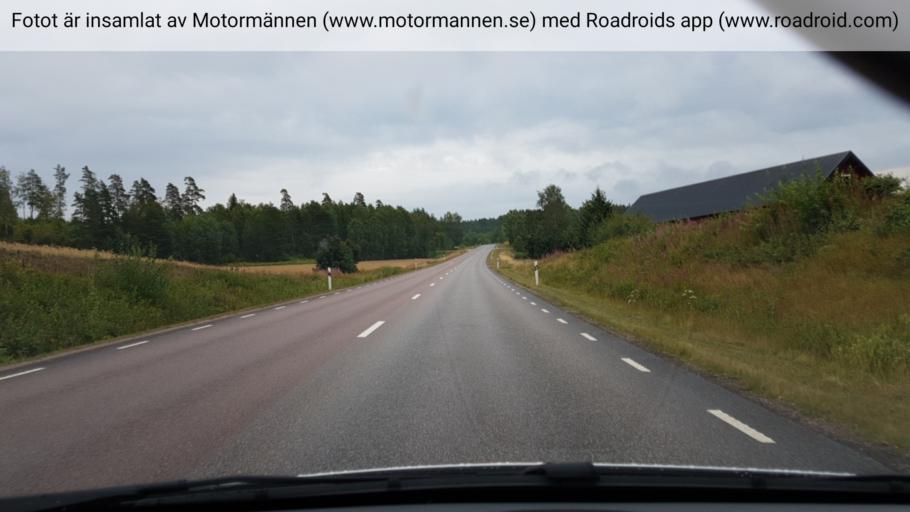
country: SE
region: Vaestra Goetaland
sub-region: Tibro Kommun
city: Tibro
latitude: 58.4547
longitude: 14.2476
